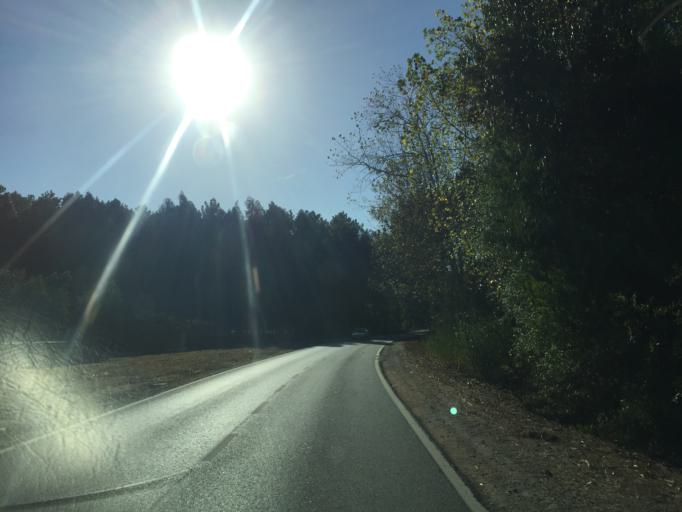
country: PT
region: Coimbra
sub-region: Figueira da Foz
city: Buarcos
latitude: 40.2157
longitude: -8.8789
